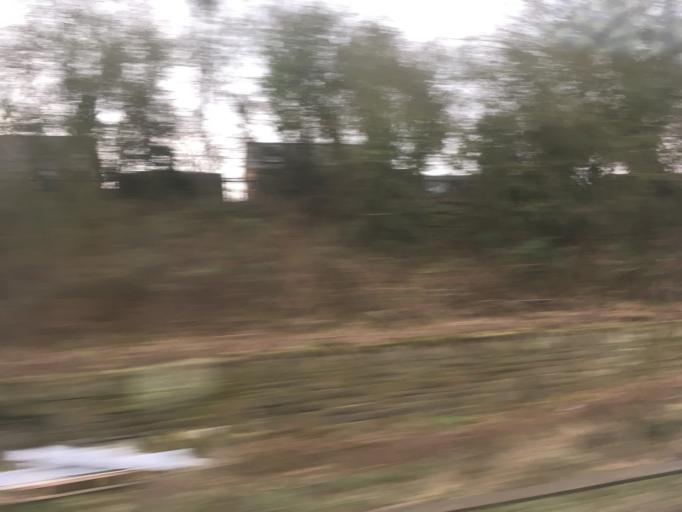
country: GB
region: England
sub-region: Wiltshire
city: Royal Wootton Bassett
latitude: 51.5343
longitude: -1.8978
